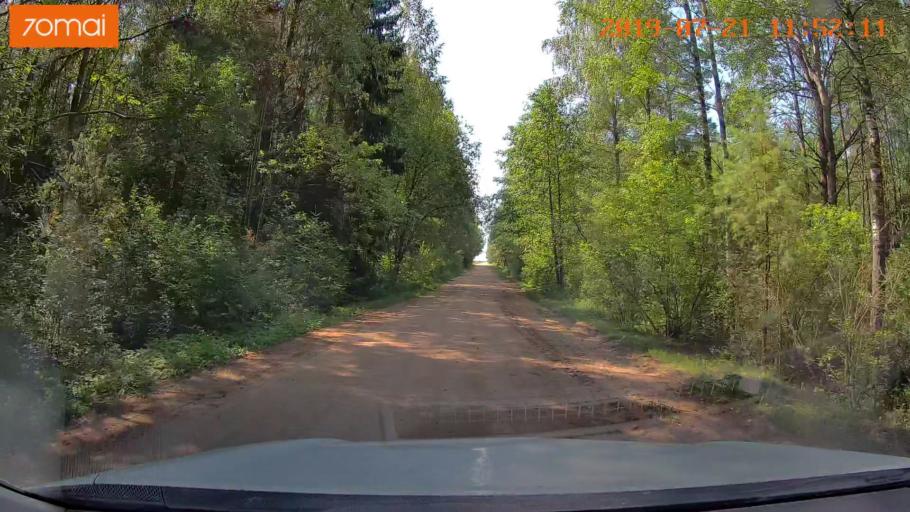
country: BY
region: Grodnenskaya
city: Lyubcha
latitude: 53.8790
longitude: 26.0087
